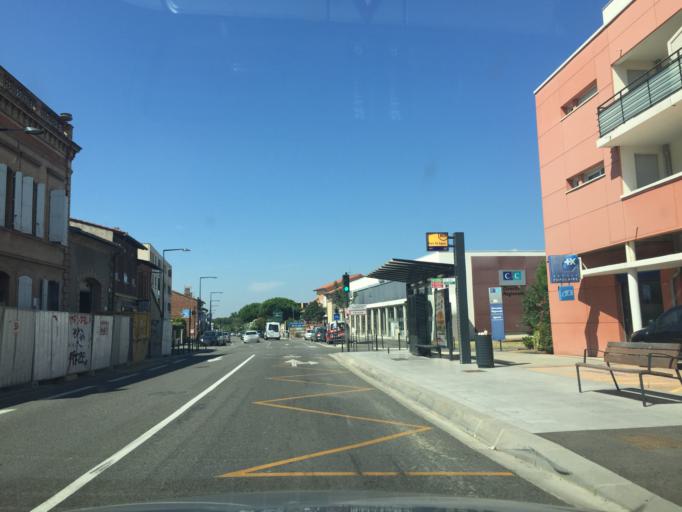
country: FR
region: Midi-Pyrenees
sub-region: Departement de la Haute-Garonne
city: Ramonville-Saint-Agne
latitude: 43.5527
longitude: 1.4690
